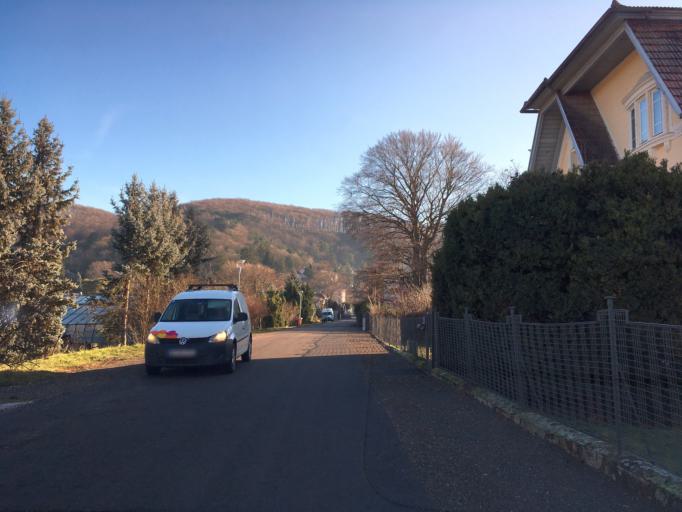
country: AT
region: Lower Austria
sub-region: Politischer Bezirk Tulln
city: Wordern
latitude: 48.3269
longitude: 16.2127
